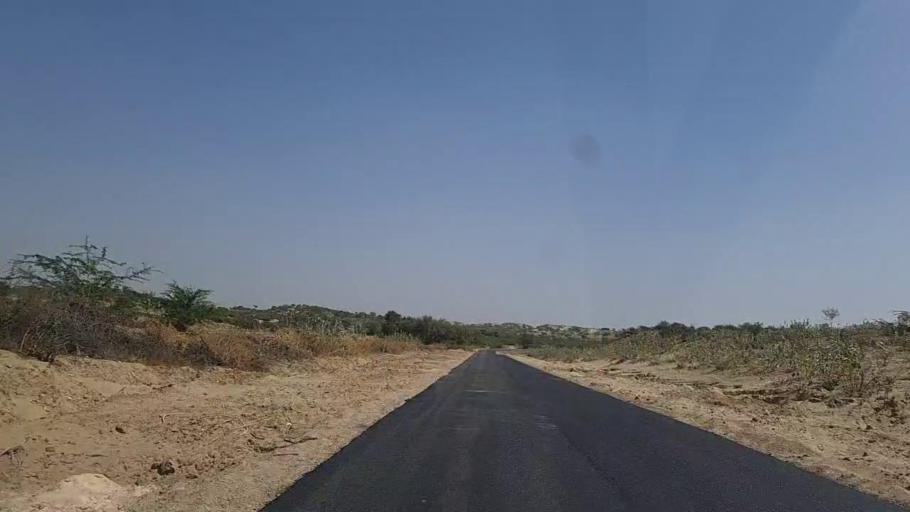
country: PK
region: Sindh
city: Diplo
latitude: 24.4807
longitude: 69.5204
